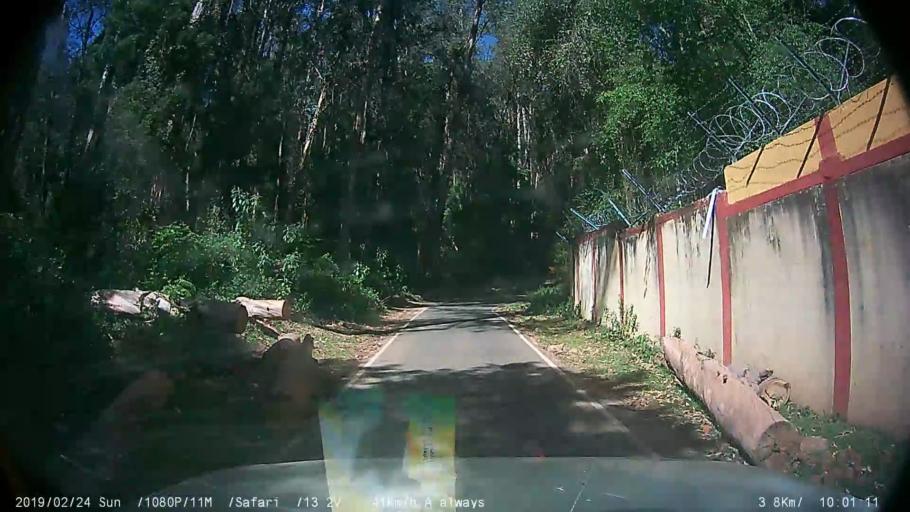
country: IN
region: Tamil Nadu
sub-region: Nilgiri
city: Aravankadu
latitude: 11.3643
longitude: 76.7583
